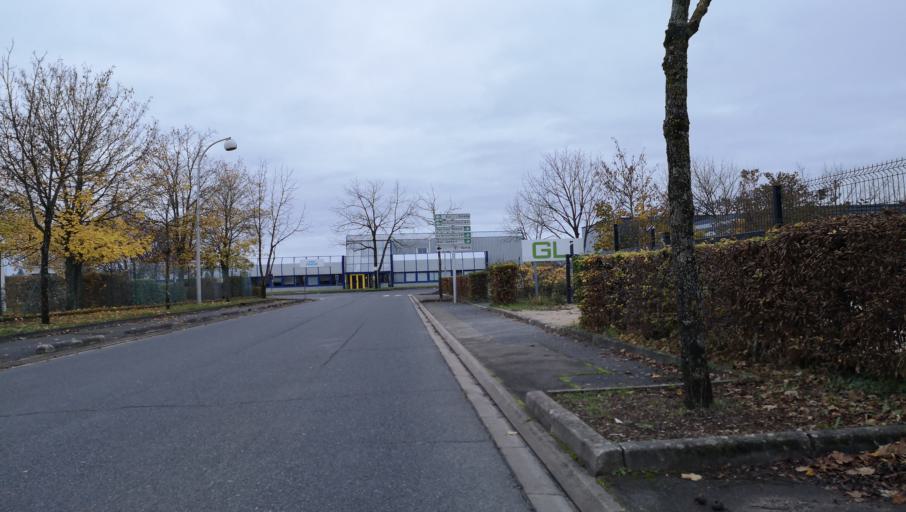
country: FR
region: Centre
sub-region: Departement du Loiret
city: Semoy
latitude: 47.9154
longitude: 1.9451
